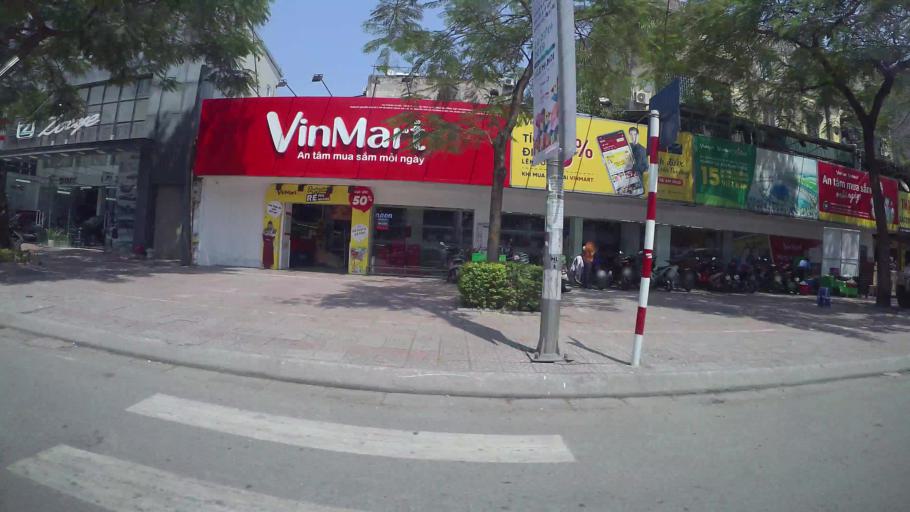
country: VN
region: Ha Noi
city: Hoan Kiem
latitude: 21.0420
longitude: 105.8700
